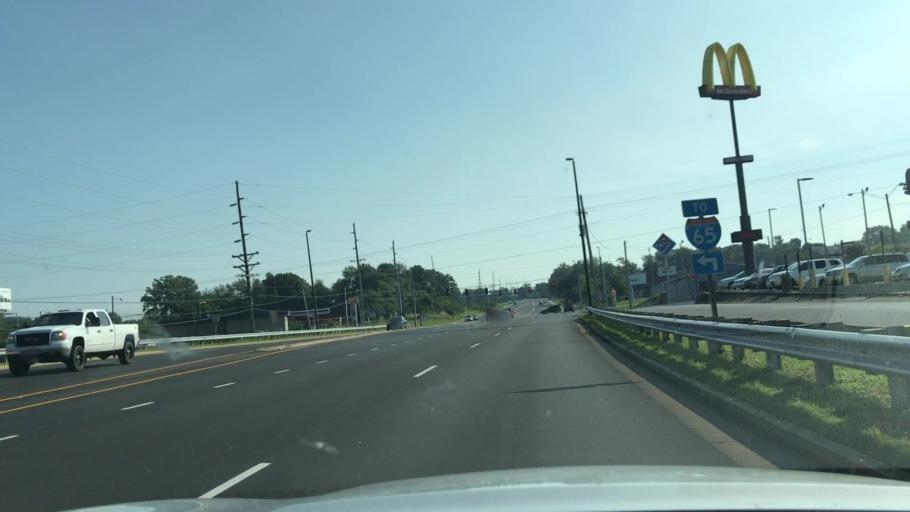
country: US
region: Kentucky
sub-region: Barren County
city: Glasgow
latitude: 37.0082
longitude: -85.9228
